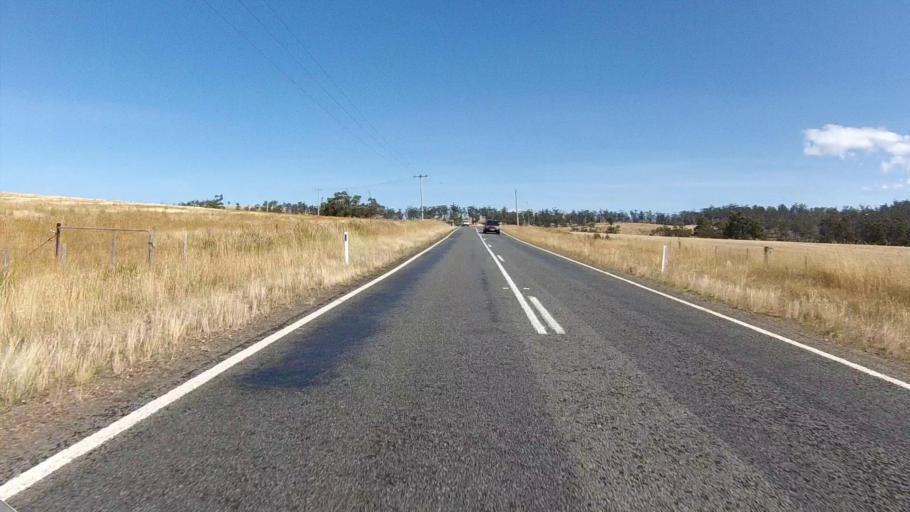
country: AU
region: Tasmania
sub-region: Sorell
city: Sorell
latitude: -42.4638
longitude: 147.9234
